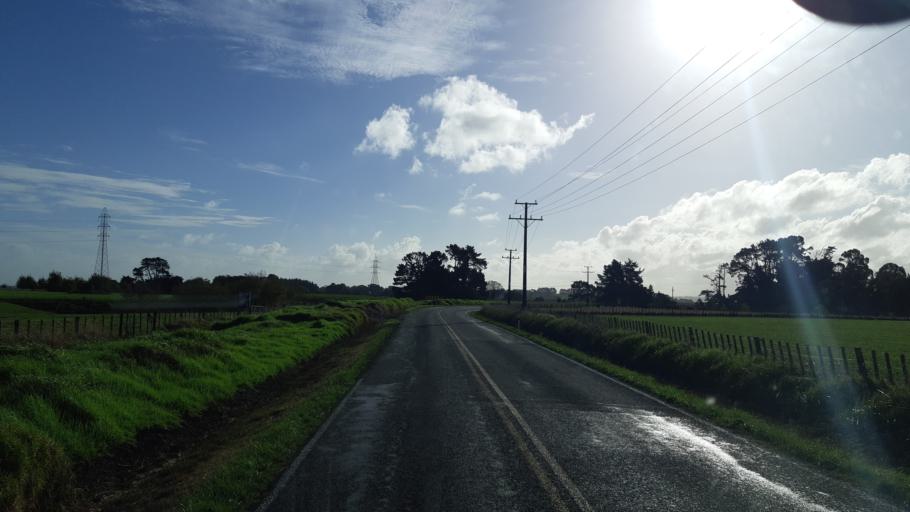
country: NZ
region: Manawatu-Wanganui
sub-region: Wanganui District
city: Wanganui
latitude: -39.9403
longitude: 175.1270
